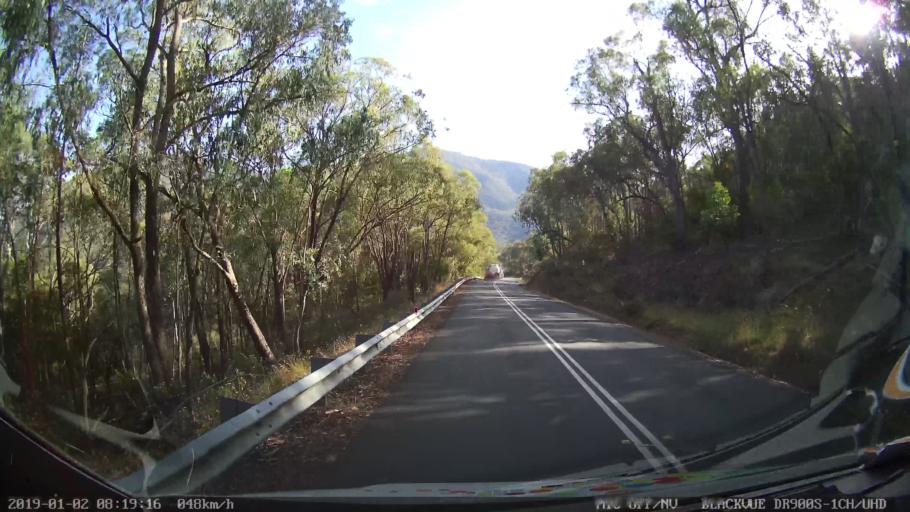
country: AU
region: New South Wales
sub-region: Tumut Shire
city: Tumut
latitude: -35.5760
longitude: 148.3204
